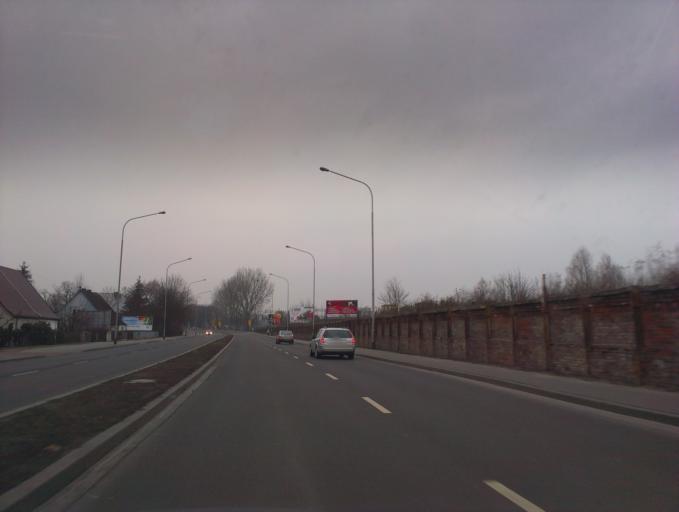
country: PL
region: Greater Poland Voivodeship
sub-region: Powiat pilski
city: Pila
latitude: 53.1414
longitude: 16.7472
